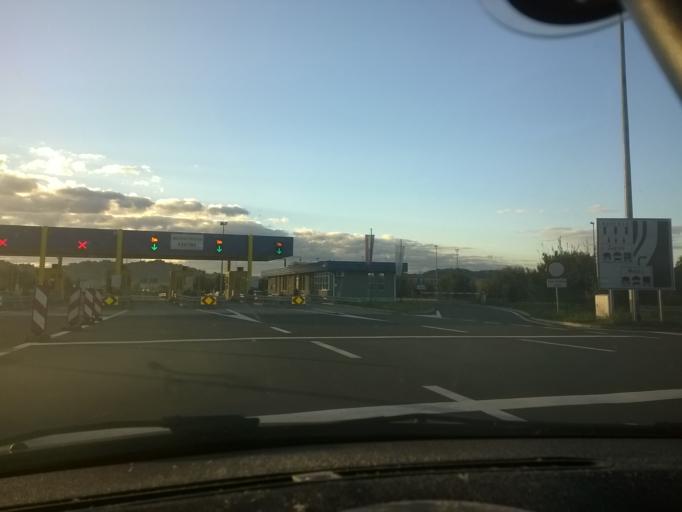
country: HR
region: Krapinsko-Zagorska
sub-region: Grad Krapina
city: Krapina
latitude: 46.1339
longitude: 15.8828
